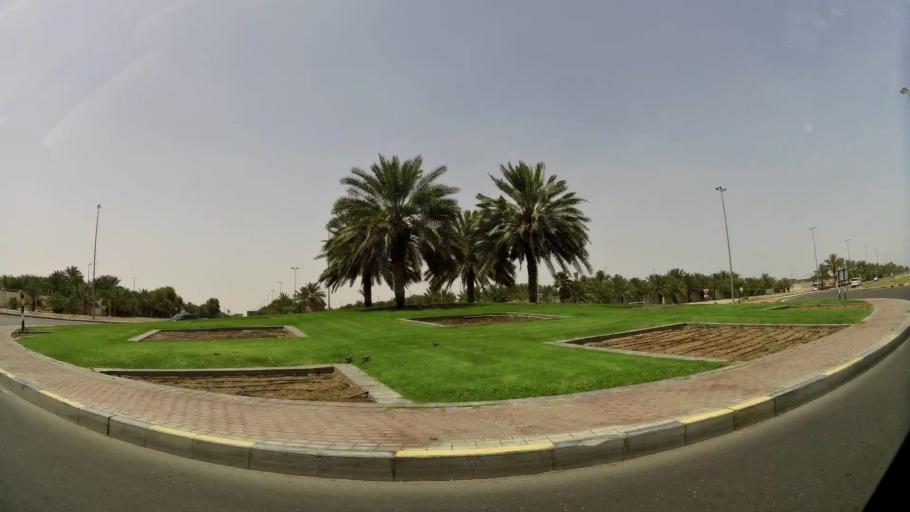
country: AE
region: Abu Dhabi
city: Al Ain
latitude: 24.1843
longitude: 55.6795
